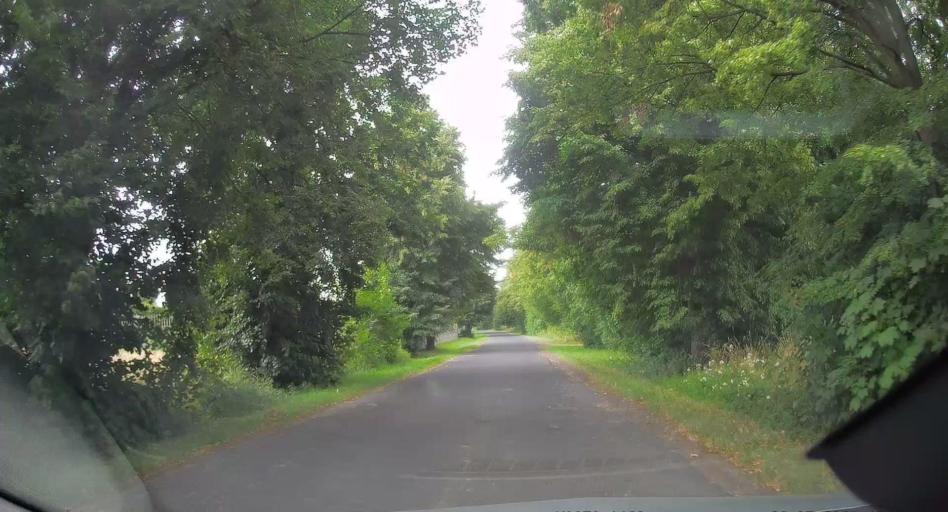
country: PL
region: Lodz Voivodeship
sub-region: Powiat rawski
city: Rawa Mazowiecka
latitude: 51.7682
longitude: 20.1835
